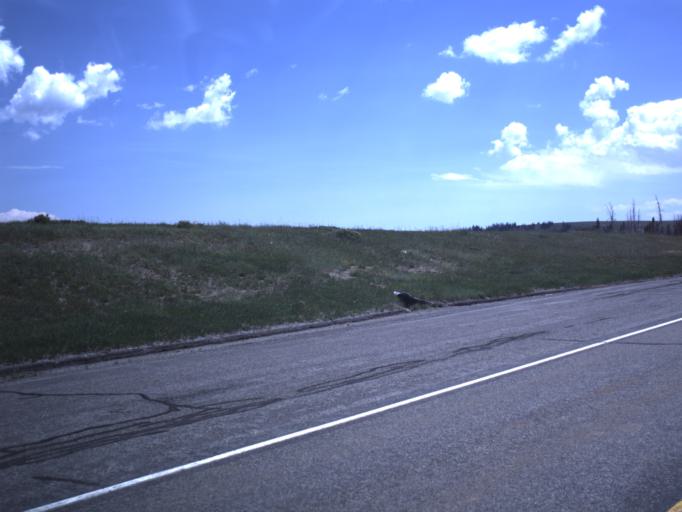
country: US
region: Utah
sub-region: Sanpete County
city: Fairview
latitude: 39.6290
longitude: -111.3230
